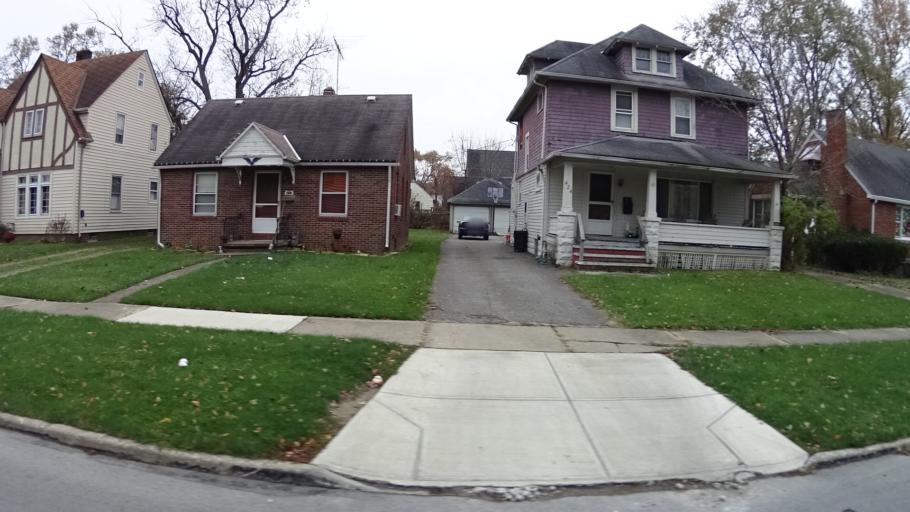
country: US
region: Ohio
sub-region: Lorain County
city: Elyria
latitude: 41.3593
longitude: -82.1116
